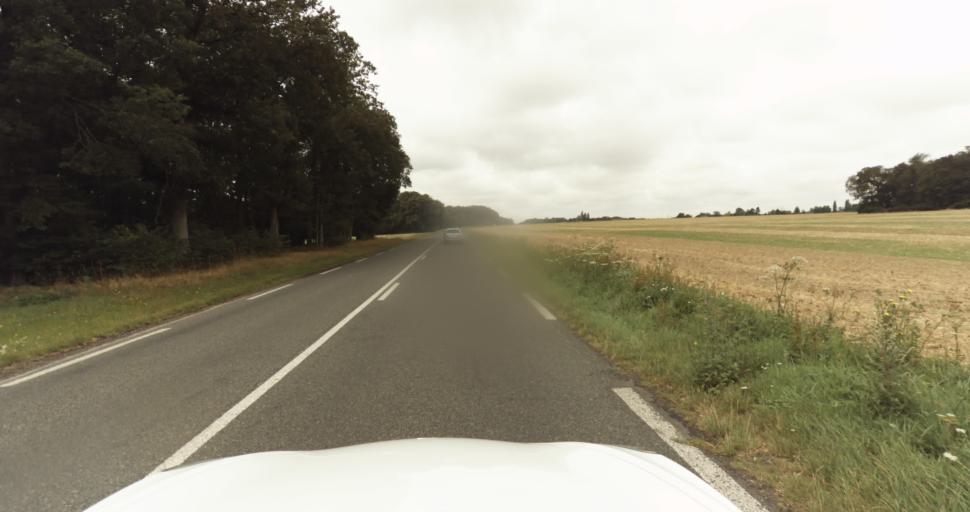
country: FR
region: Haute-Normandie
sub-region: Departement de l'Eure
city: Saint-Sebastien-de-Morsent
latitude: 49.0323
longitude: 1.0754
